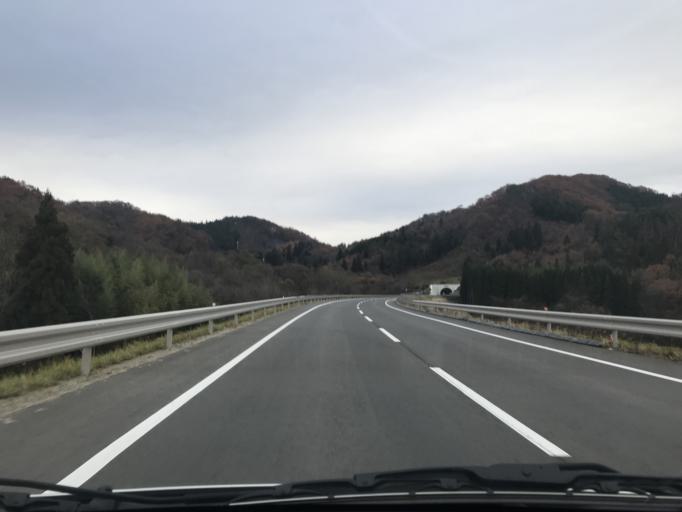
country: JP
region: Iwate
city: Kitakami
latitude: 39.2844
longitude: 141.2356
